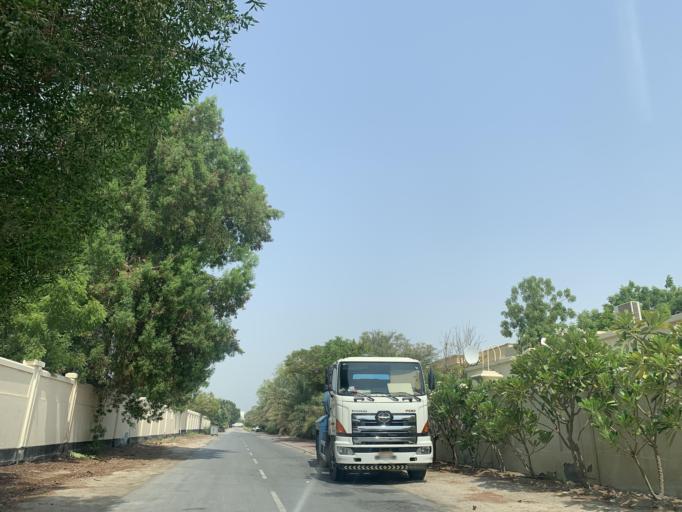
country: BH
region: Central Governorate
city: Madinat Hamad
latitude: 26.1642
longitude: 50.4665
